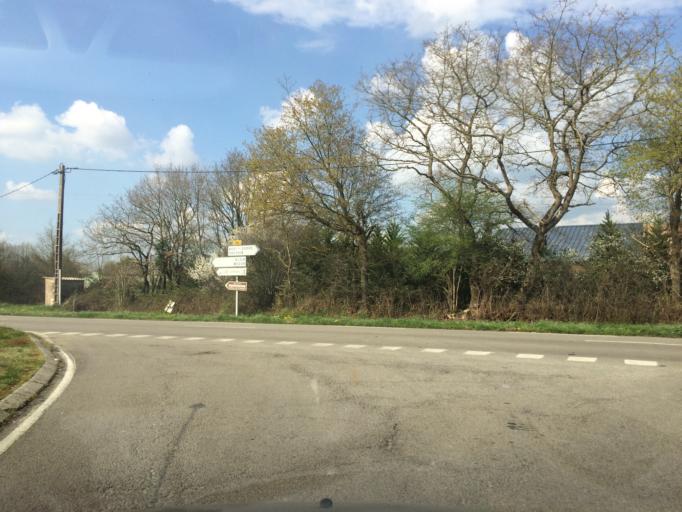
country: FR
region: Pays de la Loire
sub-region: Departement de la Loire-Atlantique
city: Heric
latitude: 47.4597
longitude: -1.6948
